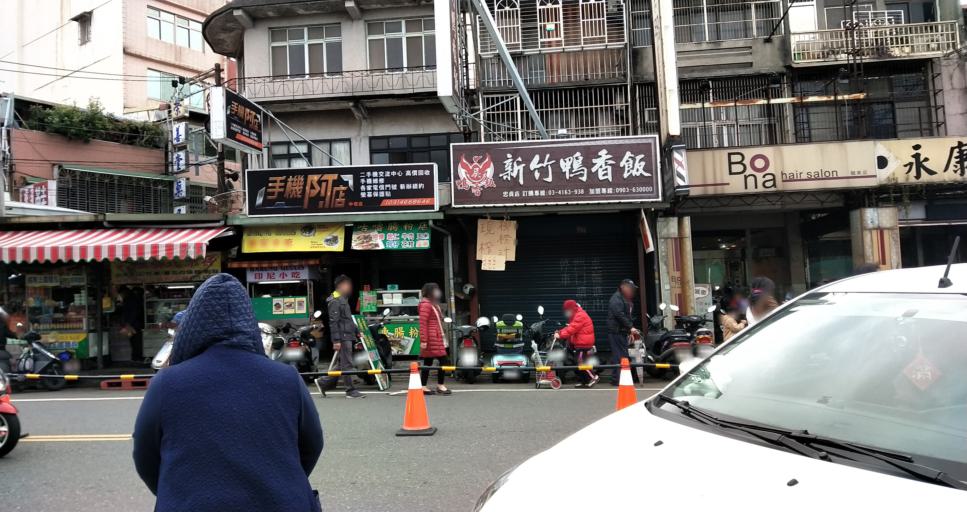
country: TW
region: Taiwan
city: Daxi
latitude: 24.9300
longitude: 121.2532
